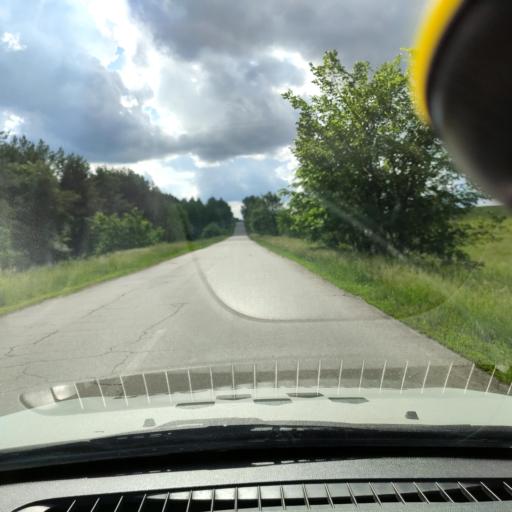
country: RU
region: Samara
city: Povolzhskiy
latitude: 53.6481
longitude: 49.7479
